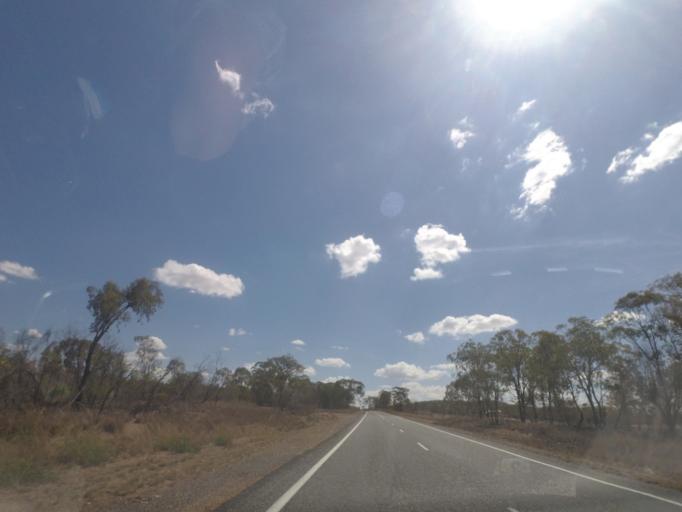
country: AU
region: Queensland
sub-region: Southern Downs
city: Warwick
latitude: -28.2182
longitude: 151.5592
